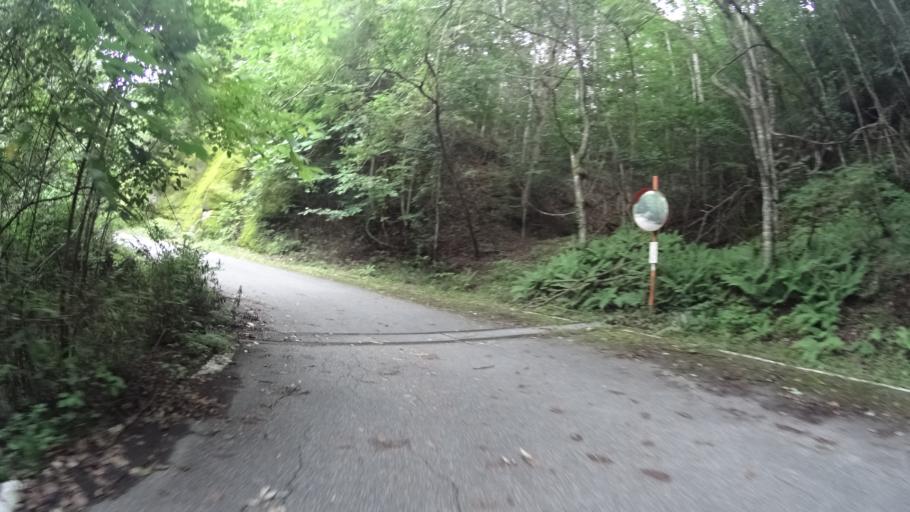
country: JP
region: Yamanashi
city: Kofu-shi
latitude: 35.8055
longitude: 138.5962
